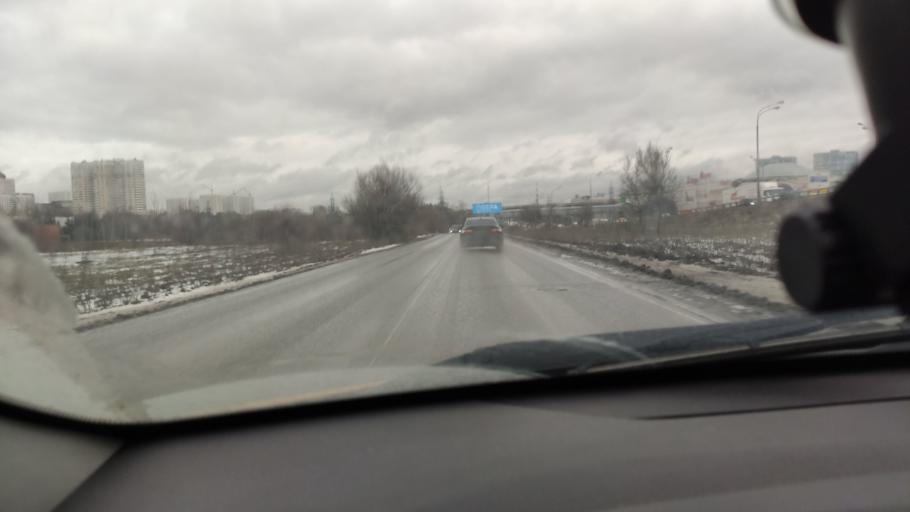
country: RU
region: Moskovskaya
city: Razvilka
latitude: 55.5874
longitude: 37.7173
